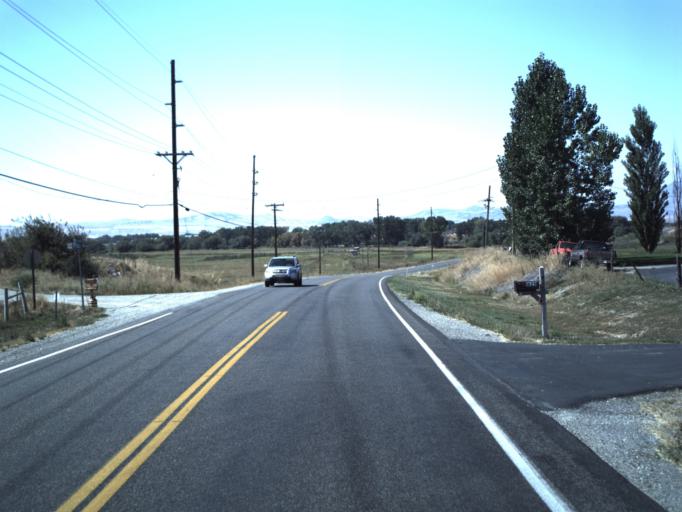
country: US
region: Utah
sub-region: Cache County
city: Smithfield
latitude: 41.8390
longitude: -111.8736
